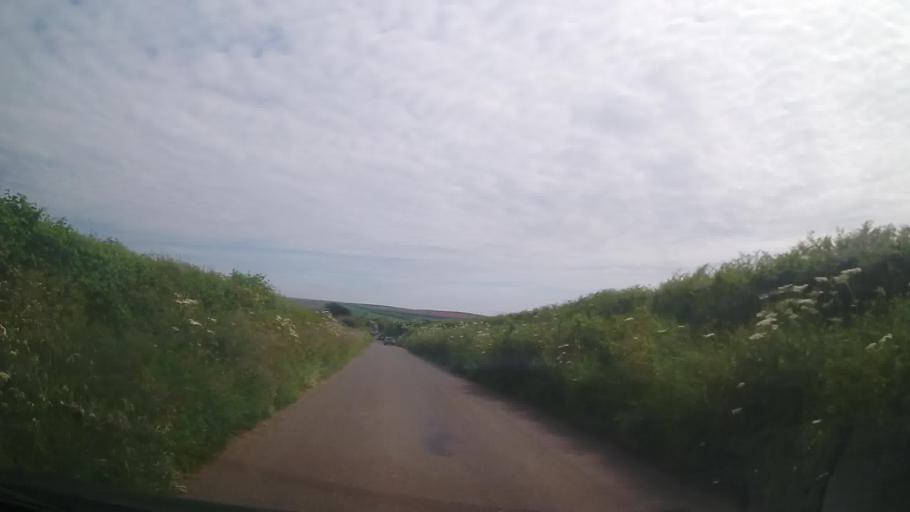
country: GB
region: England
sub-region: Devon
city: Salcombe
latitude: 50.2460
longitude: -3.6820
